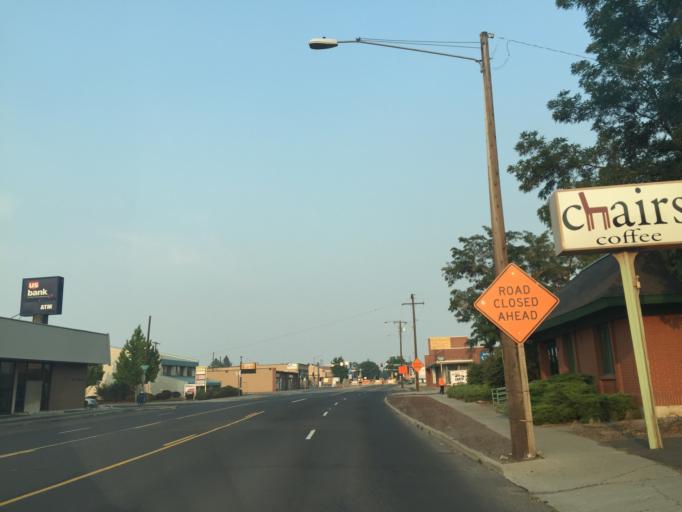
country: US
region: Washington
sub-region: Spokane County
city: Spokane
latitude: 47.6750
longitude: -117.4137
